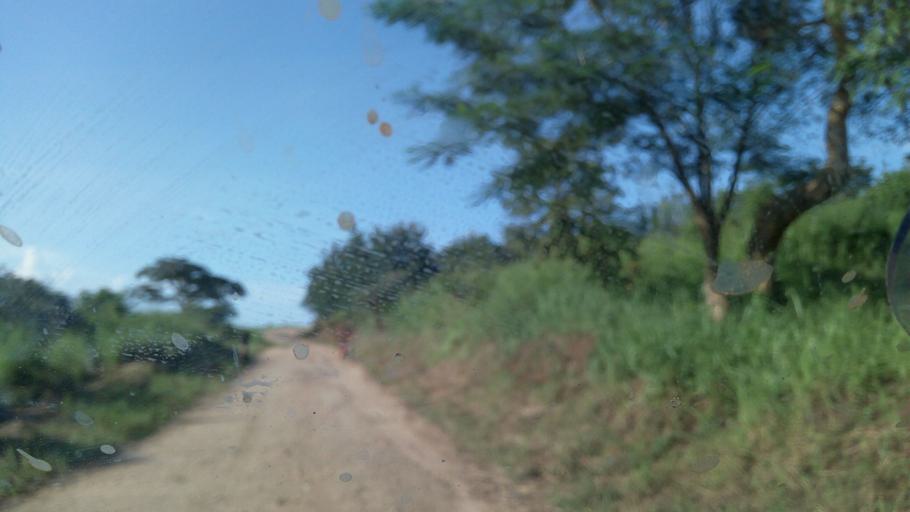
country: BI
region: Bururi
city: Rumonge
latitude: -4.2744
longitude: 28.9719
